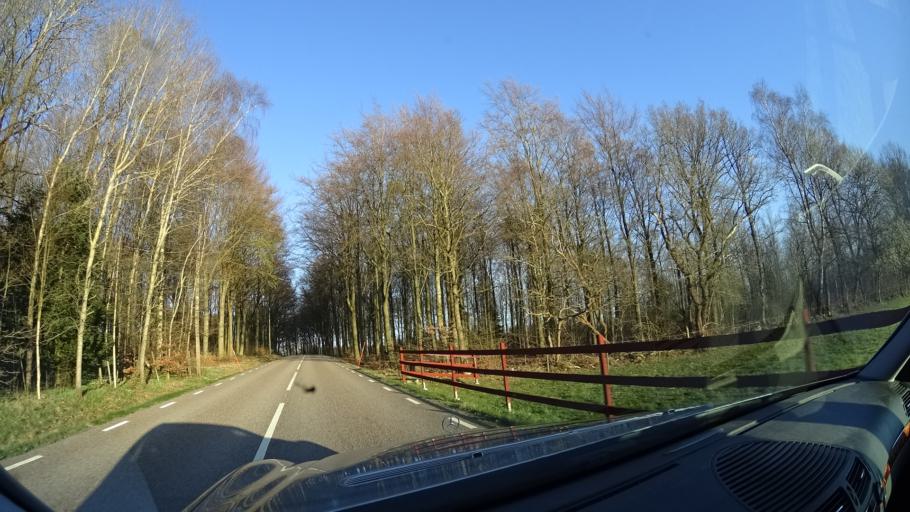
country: SE
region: Skane
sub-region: Svalovs Kommun
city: Kagerod
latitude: 55.9866
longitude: 13.1097
